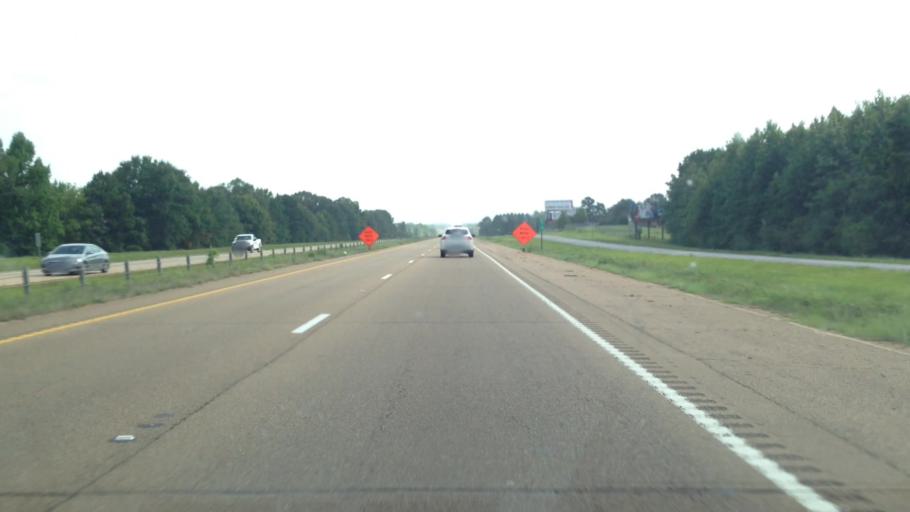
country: US
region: Mississippi
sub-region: Hinds County
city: Terry
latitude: 32.0738
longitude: -90.3166
